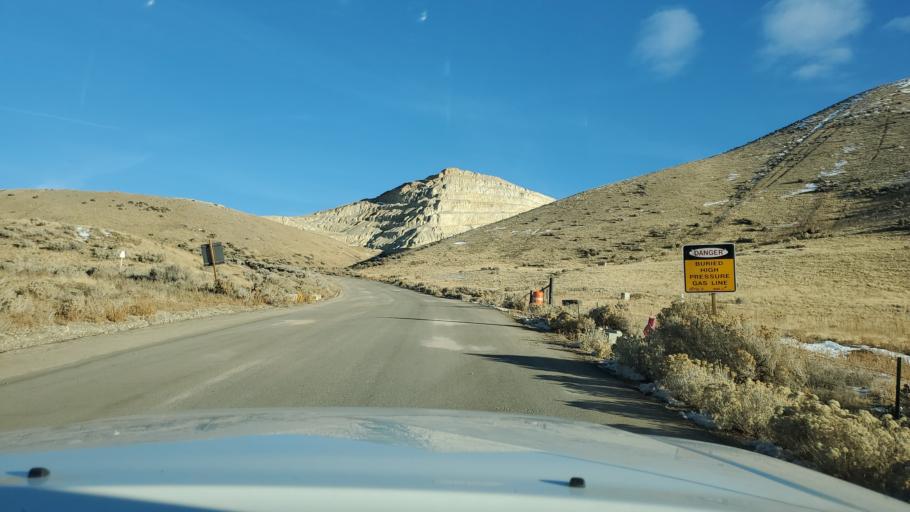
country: US
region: Utah
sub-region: Salt Lake County
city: Bluffdale
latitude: 40.4575
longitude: -111.8951
